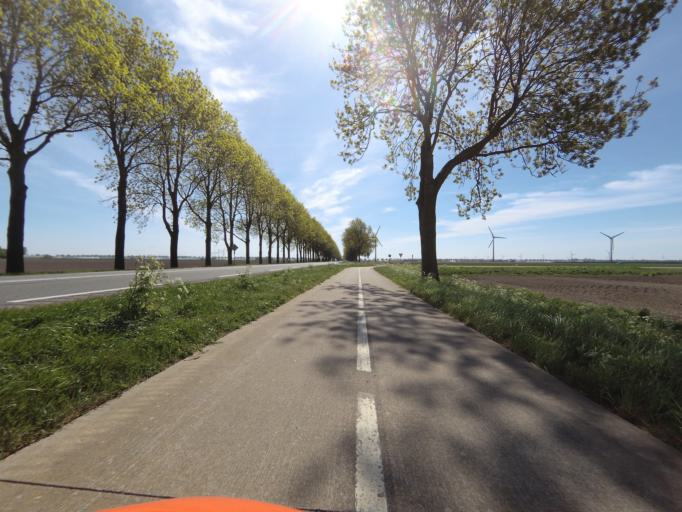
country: NL
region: Flevoland
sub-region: Gemeente Dronten
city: Biddinghuizen
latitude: 52.4943
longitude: 5.6505
